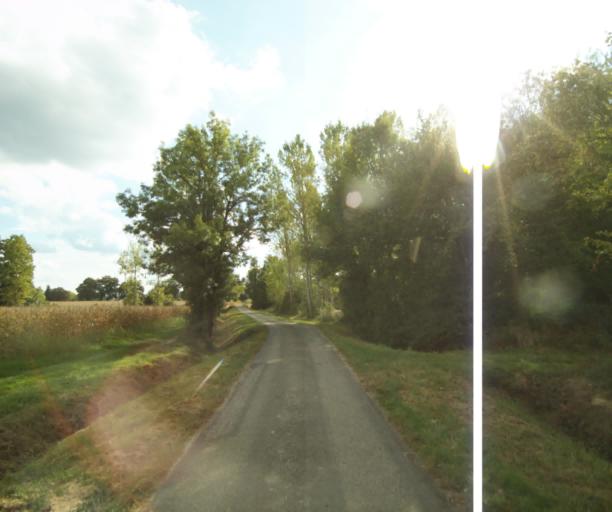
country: FR
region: Midi-Pyrenees
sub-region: Departement du Gers
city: Cazaubon
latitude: 43.9138
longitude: -0.0510
